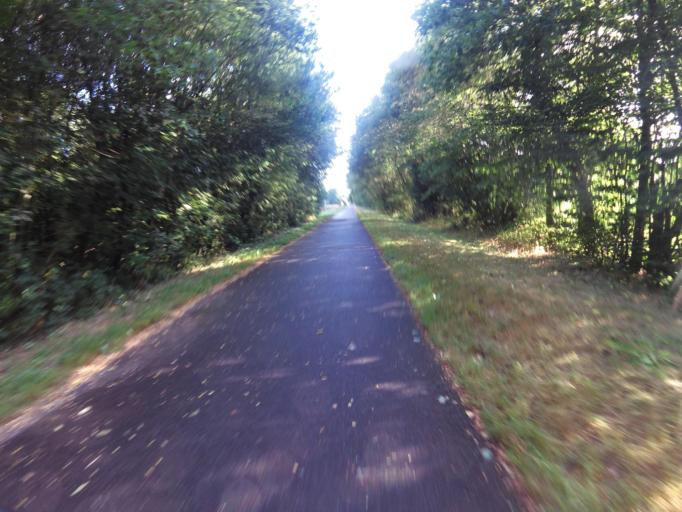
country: FR
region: Brittany
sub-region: Departement du Morbihan
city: Guillac
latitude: 47.8763
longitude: -2.4373
